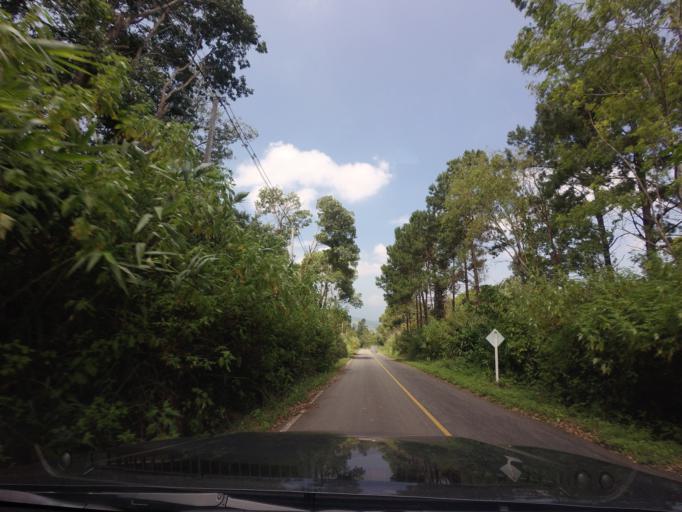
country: TH
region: Loei
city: Na Haeo
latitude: 17.4866
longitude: 100.9046
